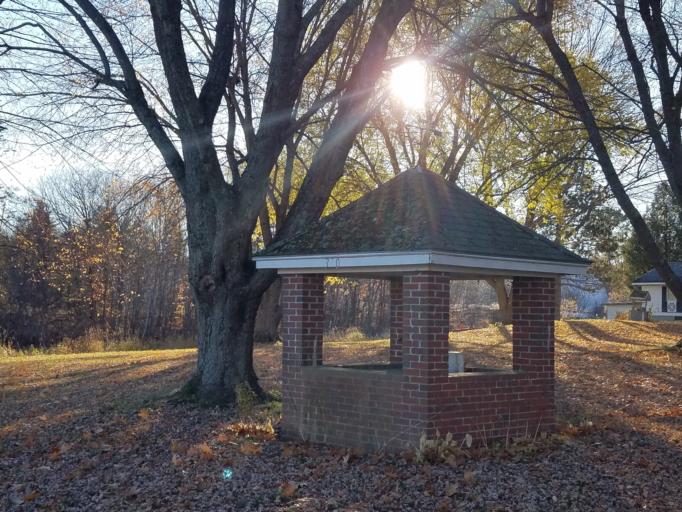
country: US
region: Maine
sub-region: Waldo County
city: Troy
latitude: 44.6796
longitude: -69.2714
